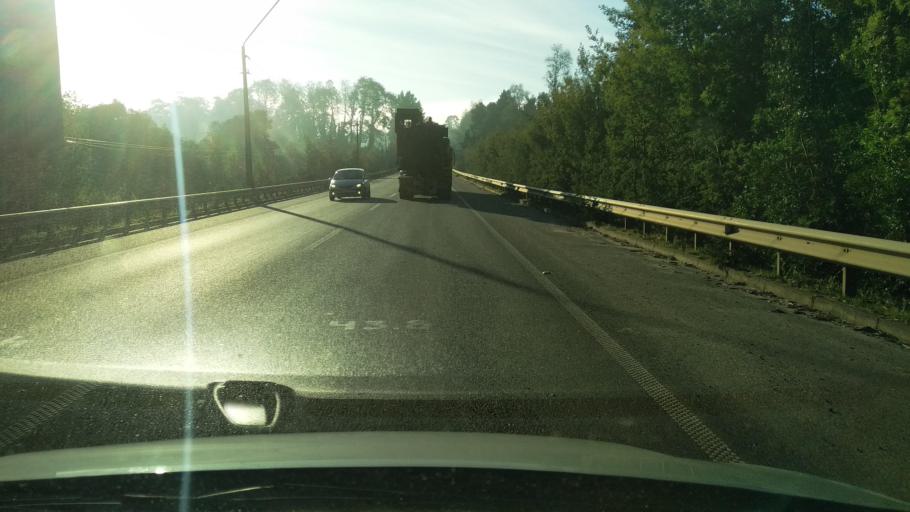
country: CL
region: Los Lagos
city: Las Animas
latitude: -39.7812
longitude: -73.2149
